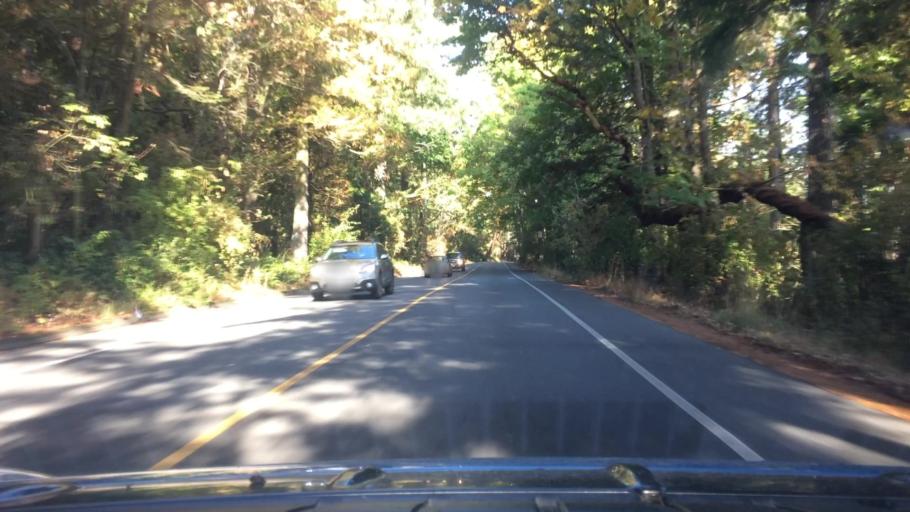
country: CA
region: British Columbia
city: Oak Bay
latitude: 48.5001
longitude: -123.3408
